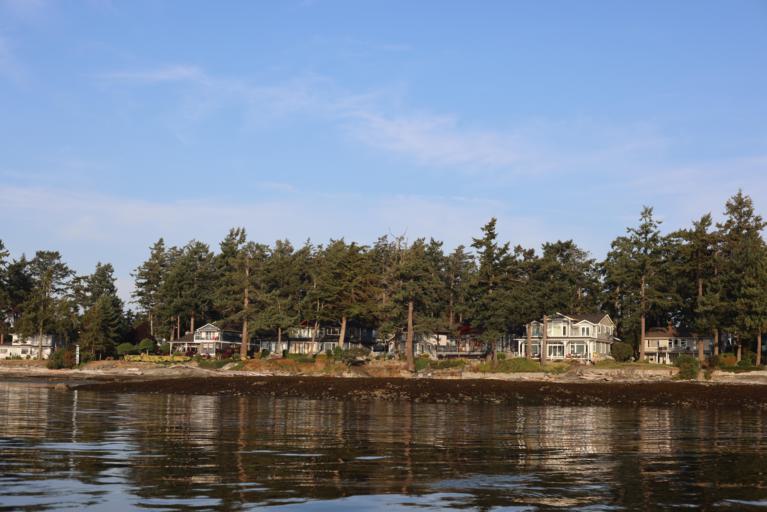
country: CA
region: British Columbia
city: North Saanich
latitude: 48.6611
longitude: -123.3903
